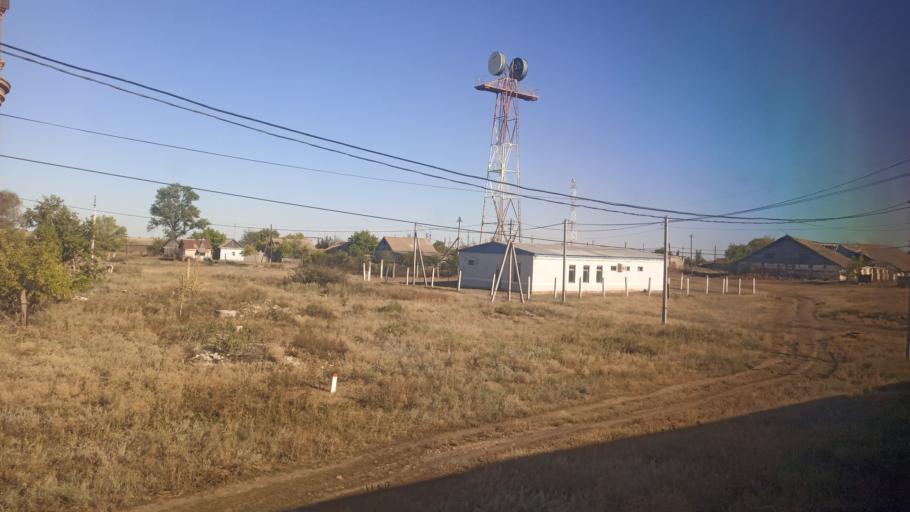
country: RU
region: Saratov
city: Krasnyy Kut
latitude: 50.6563
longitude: 46.9213
